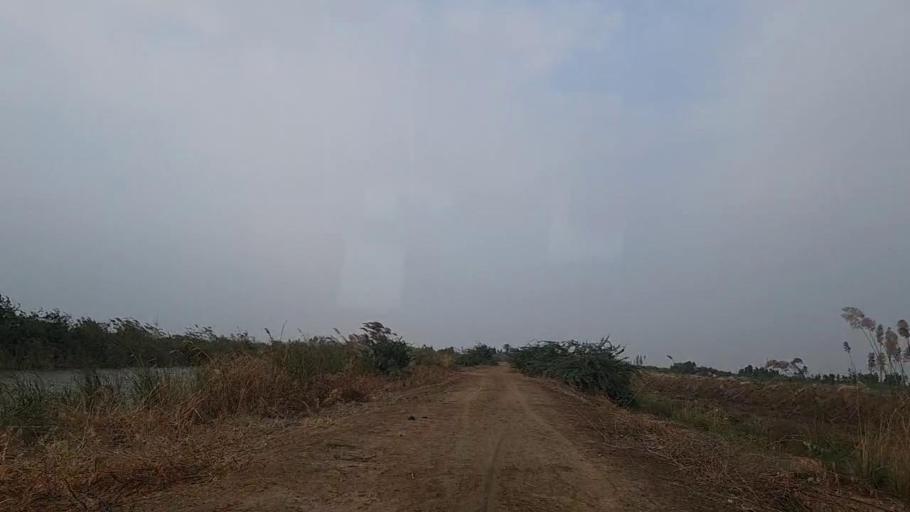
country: PK
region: Sindh
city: Gharo
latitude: 24.6242
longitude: 67.5025
